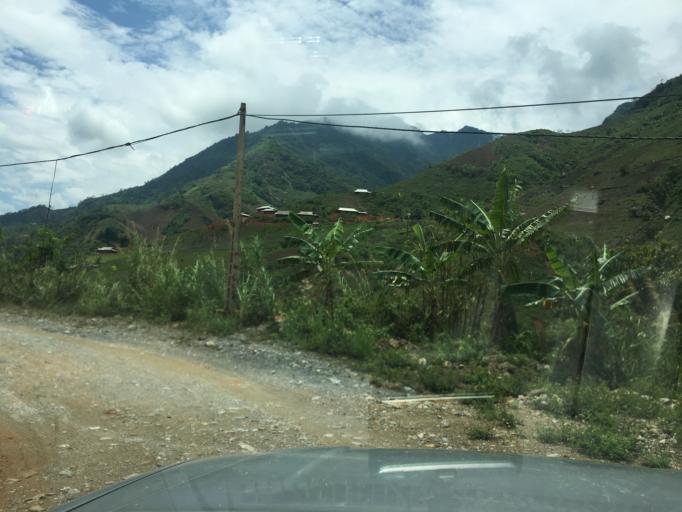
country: VN
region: Yen Bai
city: Son Thinh
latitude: 21.6774
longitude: 104.5395
